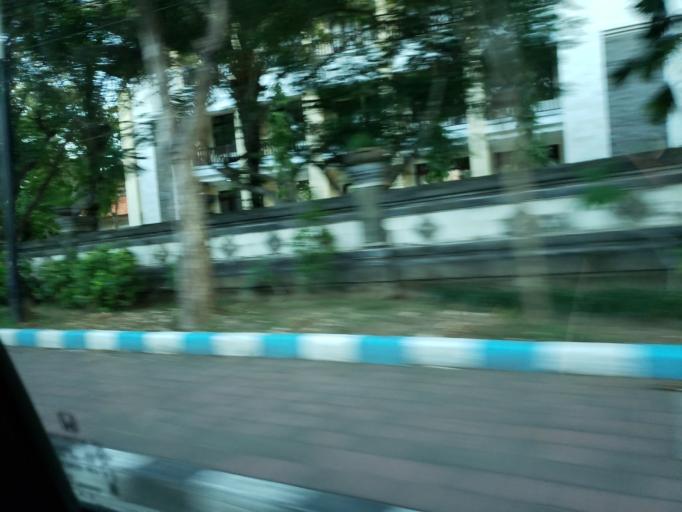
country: ID
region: Bali
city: Jimbaran
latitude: -8.7988
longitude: 115.1630
